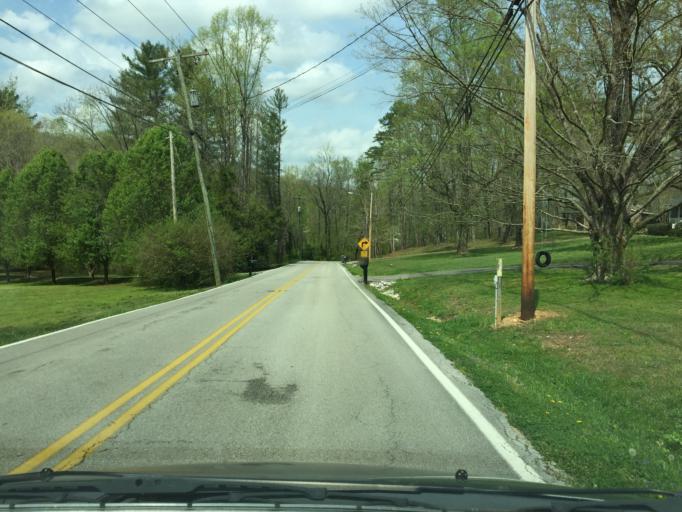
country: US
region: Tennessee
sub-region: Hamilton County
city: Walden
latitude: 35.1606
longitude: -85.2777
